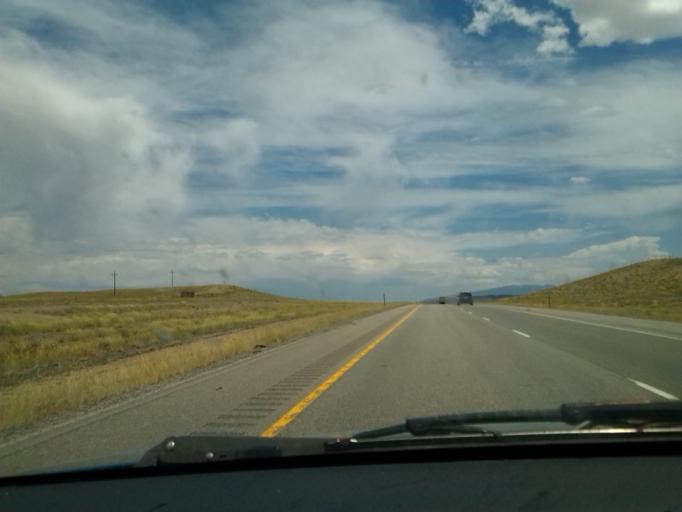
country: US
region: Wyoming
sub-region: Carbon County
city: Rawlins
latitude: 41.7572
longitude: -106.9793
